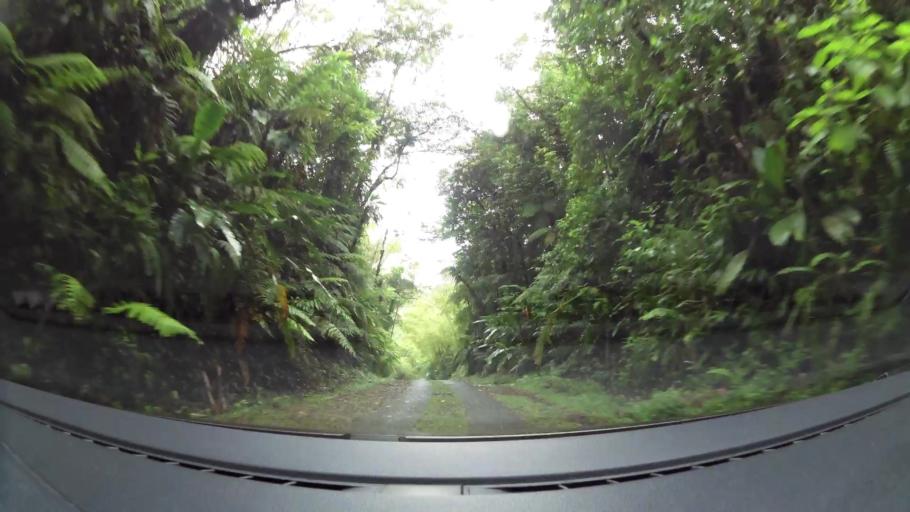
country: GP
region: Guadeloupe
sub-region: Guadeloupe
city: Trois-Rivieres
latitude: 16.0369
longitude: -61.6368
